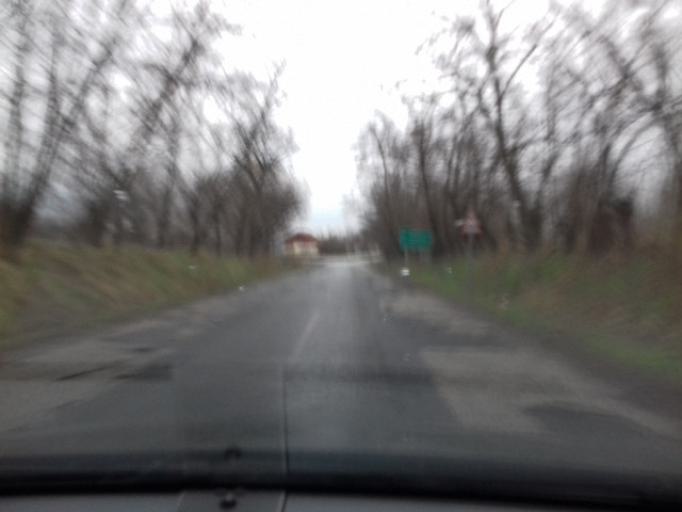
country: HU
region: Szabolcs-Szatmar-Bereg
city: Nyirbogdany
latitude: 48.0654
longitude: 21.8605
